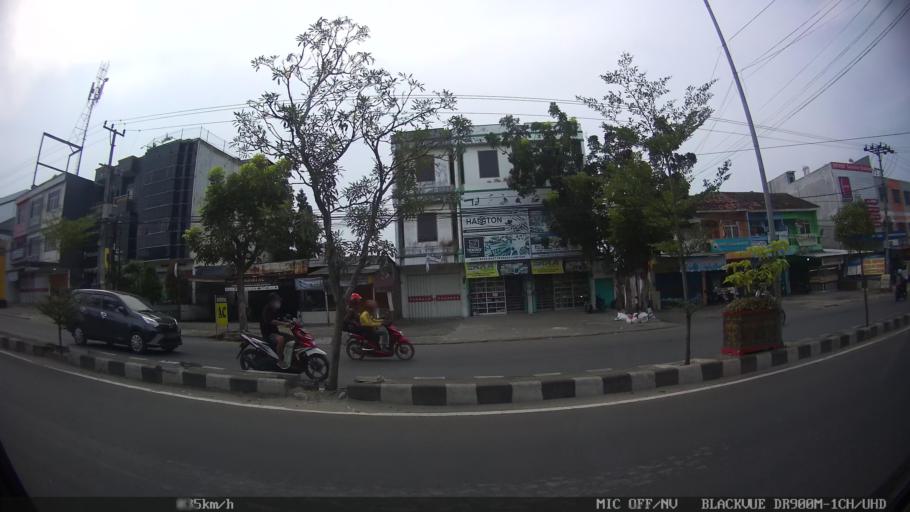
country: ID
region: Lampung
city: Kedaton
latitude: -5.3997
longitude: 105.2873
